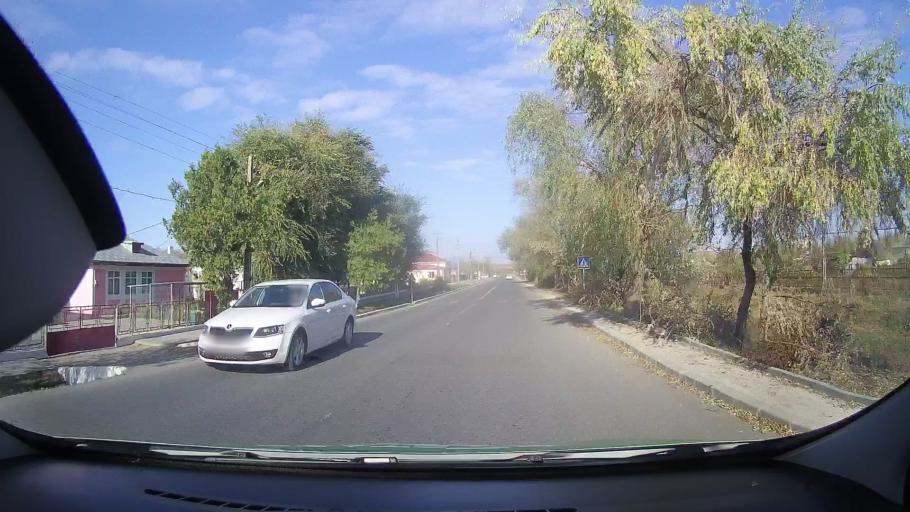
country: RO
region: Tulcea
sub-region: Comuna Valea Nucarilor
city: Valea Nucarilor
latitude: 45.0401
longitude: 28.9368
